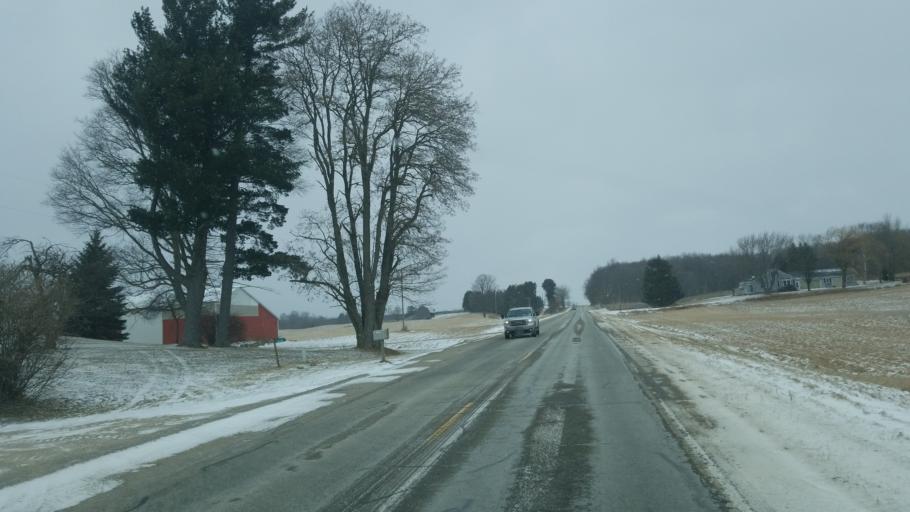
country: US
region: Michigan
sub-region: Osceola County
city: Evart
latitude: 44.0021
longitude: -85.2463
